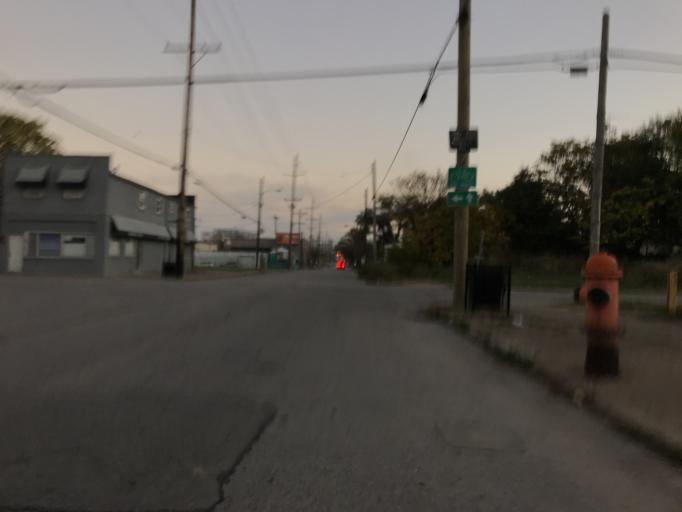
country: US
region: Kentucky
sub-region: Jefferson County
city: Louisville
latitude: 38.2428
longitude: -85.7419
